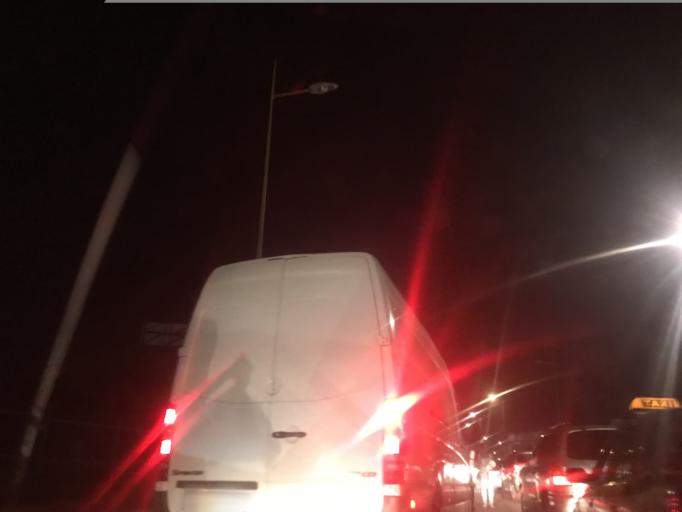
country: SN
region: Dakar
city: Grand Dakar
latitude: 14.7421
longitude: -17.4382
